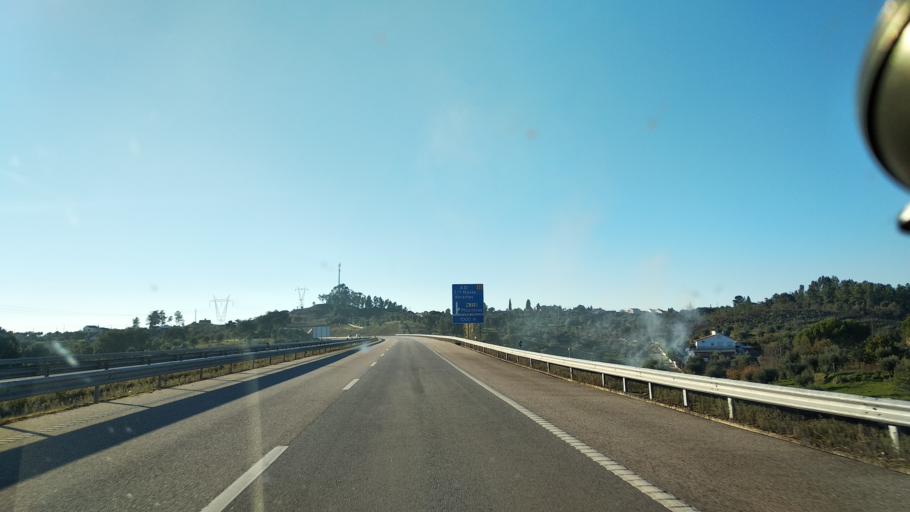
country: PT
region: Santarem
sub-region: Abrantes
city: Alferrarede
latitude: 39.4963
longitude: -8.0840
